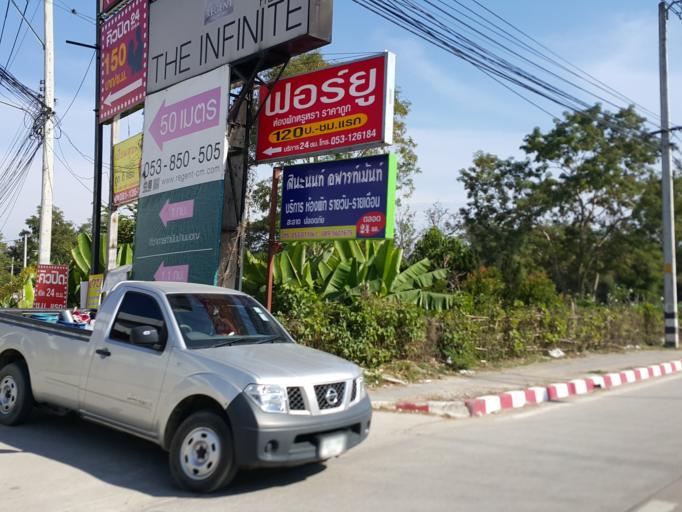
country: TH
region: Chiang Mai
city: Chiang Mai
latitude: 18.7921
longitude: 99.0382
